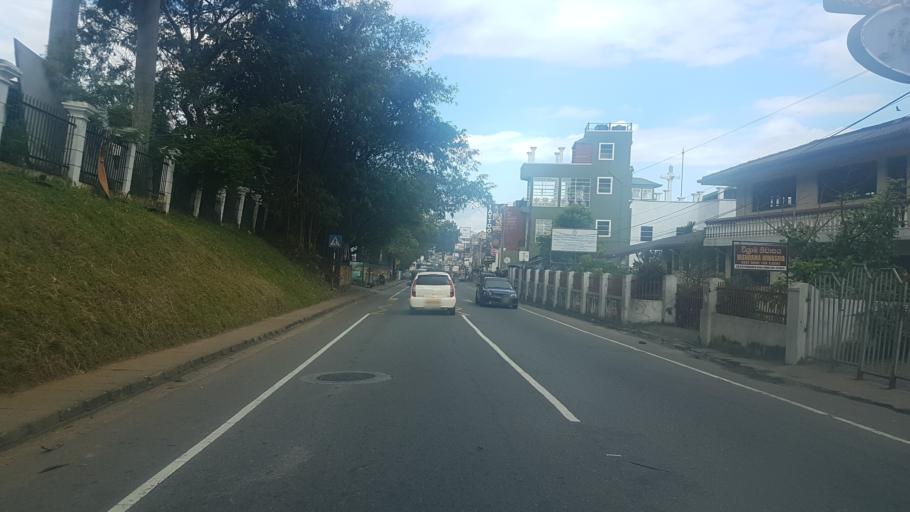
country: LK
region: Central
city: Kandy
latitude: 7.2773
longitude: 80.6157
